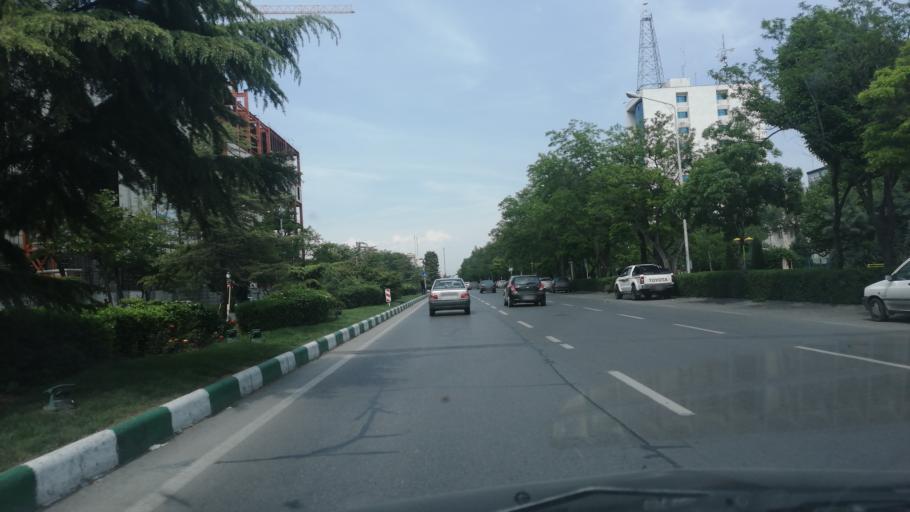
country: IR
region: Razavi Khorasan
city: Mashhad
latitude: 36.3165
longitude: 59.5621
